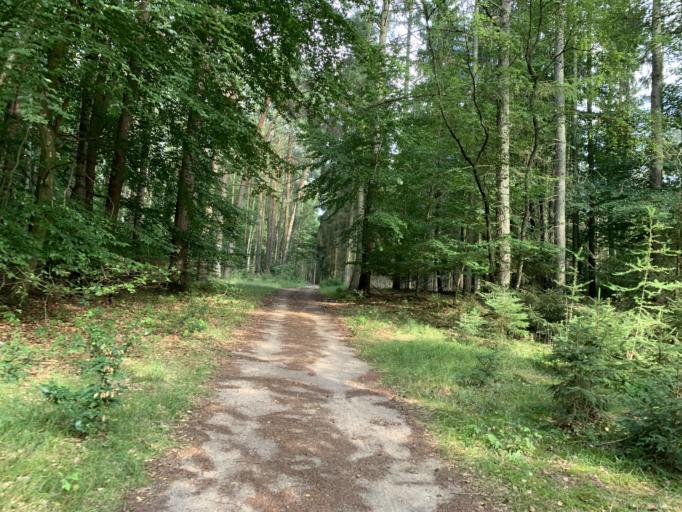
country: DE
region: Mecklenburg-Vorpommern
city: Carpin
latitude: 53.3491
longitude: 13.2268
